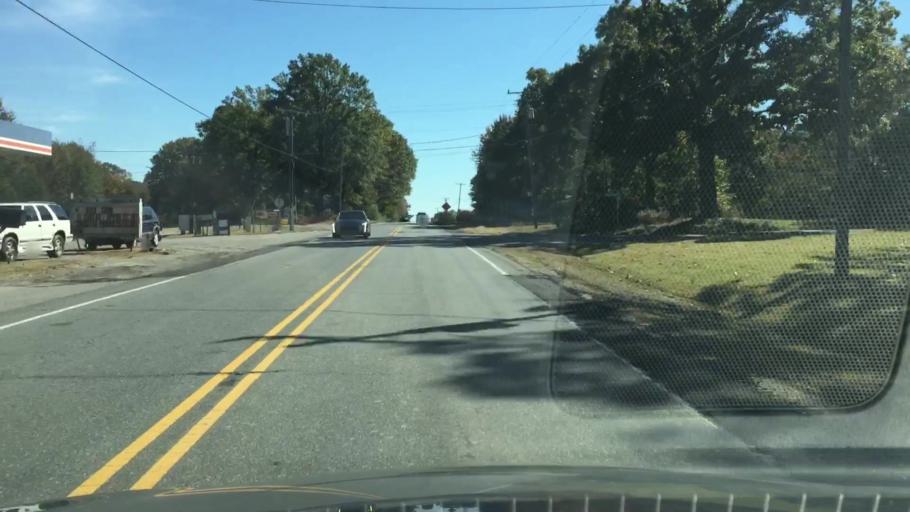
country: US
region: North Carolina
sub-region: Rockingham County
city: Reidsville
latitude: 36.2968
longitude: -79.6622
